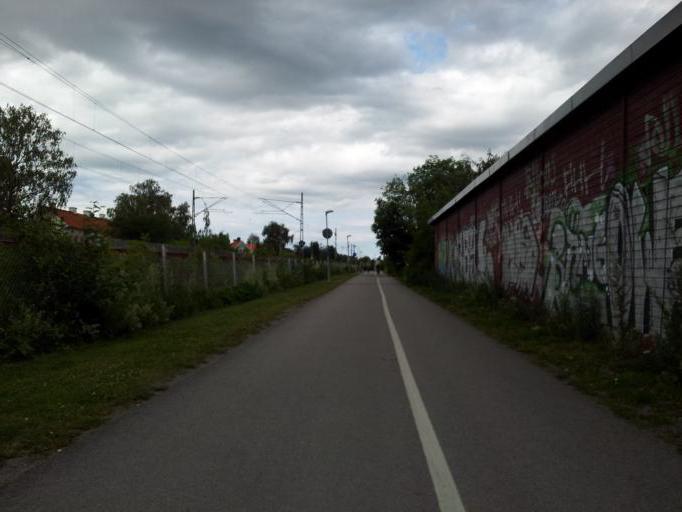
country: SE
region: Uppsala
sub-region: Uppsala Kommun
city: Uppsala
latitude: 59.8676
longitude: 17.6361
